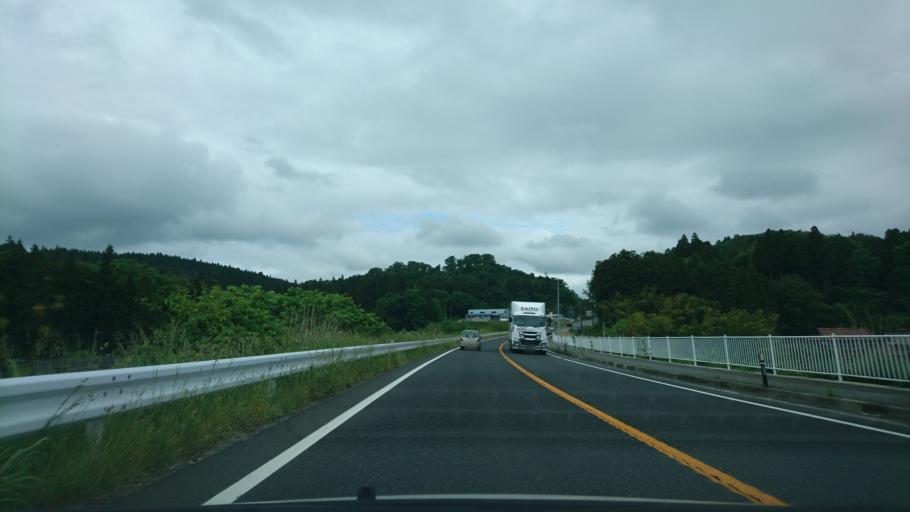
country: JP
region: Iwate
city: Ichinoseki
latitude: 38.8896
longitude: 141.1170
